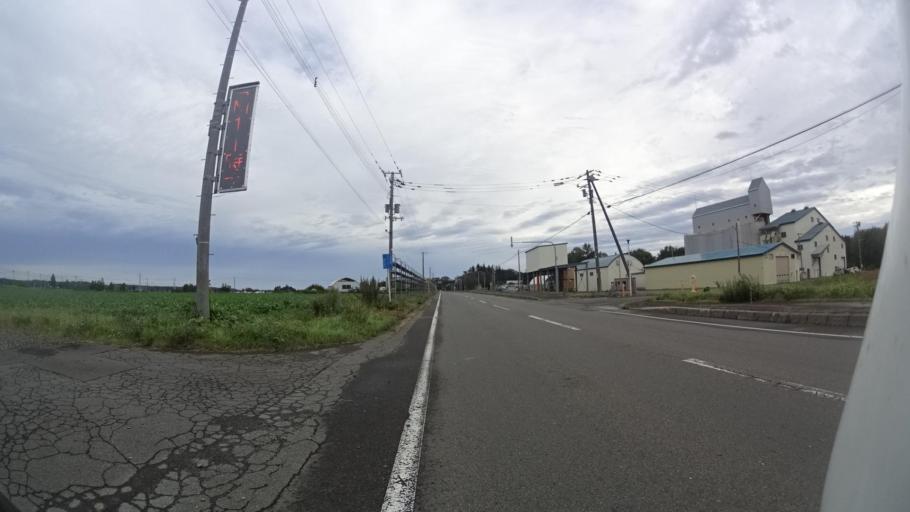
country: JP
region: Hokkaido
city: Abashiri
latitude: 43.8458
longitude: 144.5976
